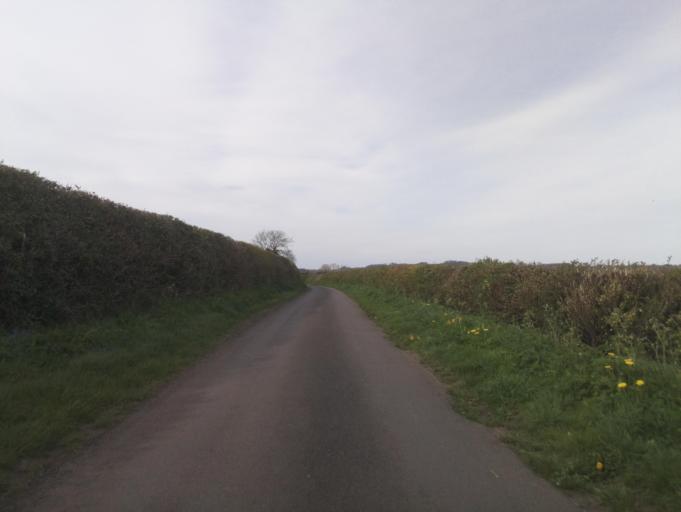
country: GB
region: England
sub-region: Somerset
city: Milborne Port
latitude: 50.9774
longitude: -2.4694
